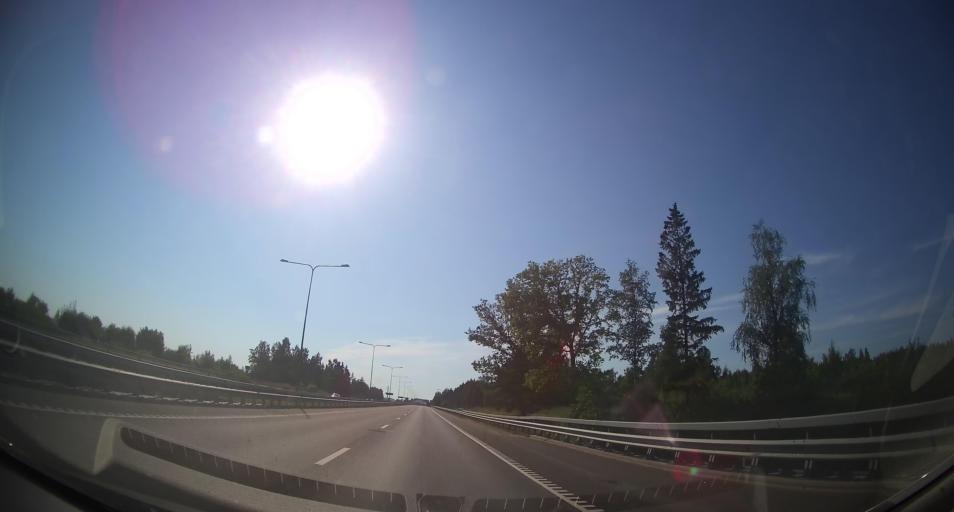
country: EE
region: Harju
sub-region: Maardu linn
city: Maardu
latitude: 59.4534
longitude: 25.0350
